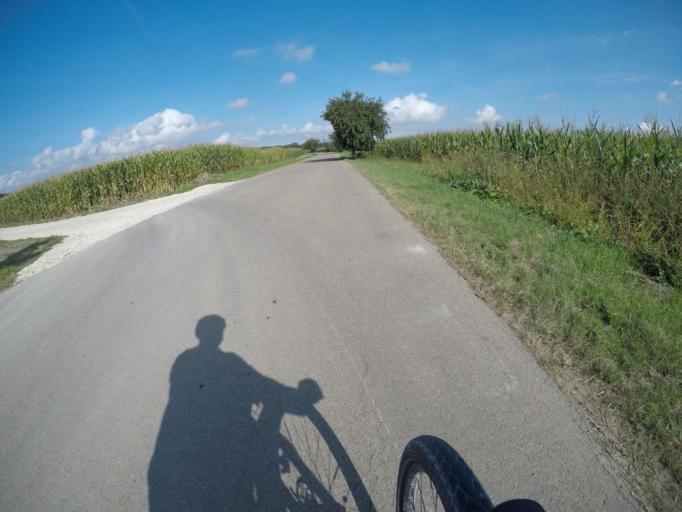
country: DE
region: Bavaria
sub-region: Swabia
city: Buttenwiesen
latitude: 48.6417
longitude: 10.7363
